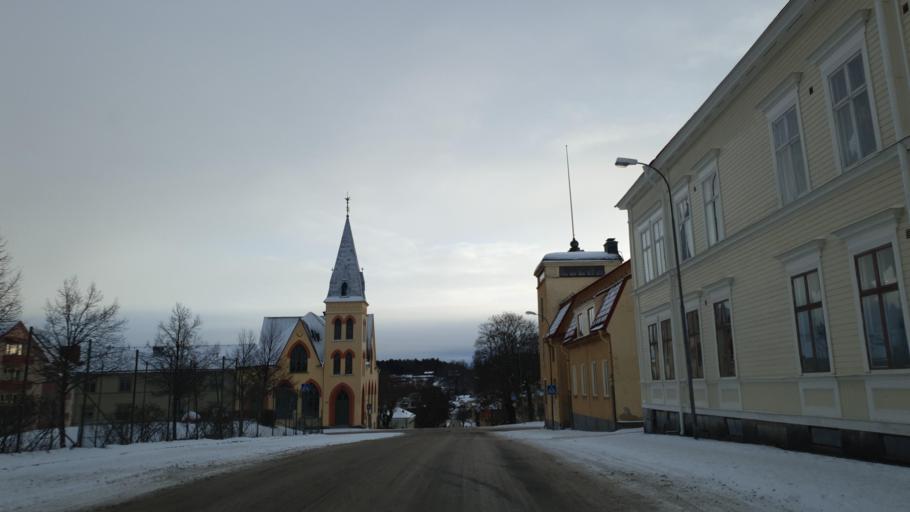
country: SE
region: Gaevleborg
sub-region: Soderhamns Kommun
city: Soderhamn
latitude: 61.3055
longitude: 17.0546
